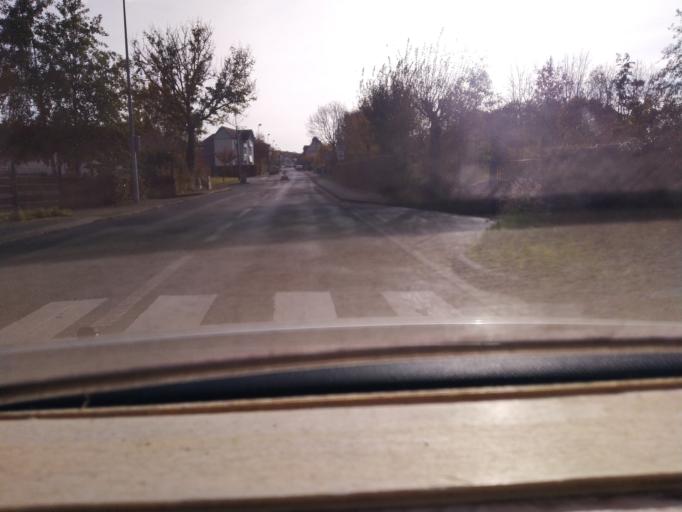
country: FR
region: Haute-Normandie
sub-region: Departement de la Seine-Maritime
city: Yainville
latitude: 49.4569
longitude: 0.8273
